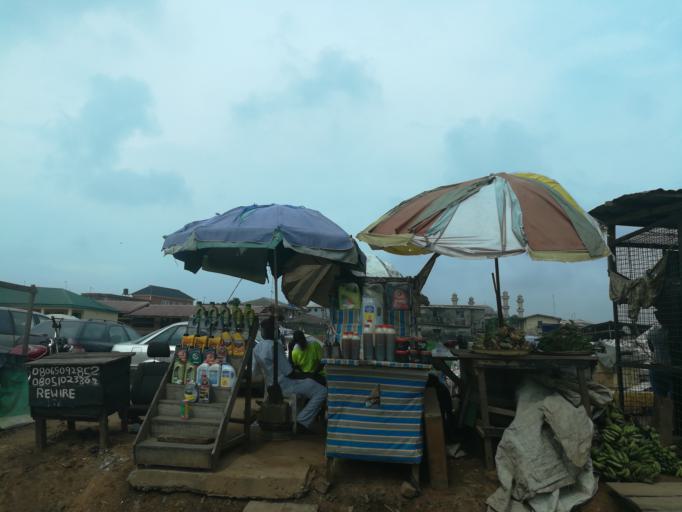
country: NG
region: Lagos
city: Ikorodu
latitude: 6.6207
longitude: 3.5071
